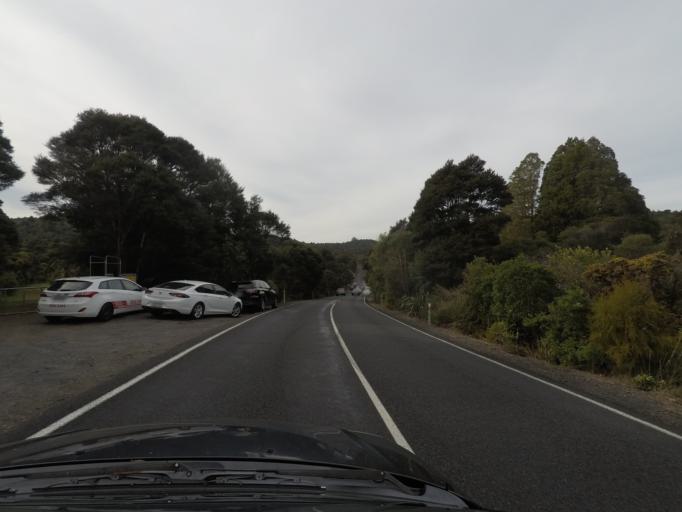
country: NZ
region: Auckland
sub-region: Auckland
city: Titirangi
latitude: -36.9368
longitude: 174.5564
